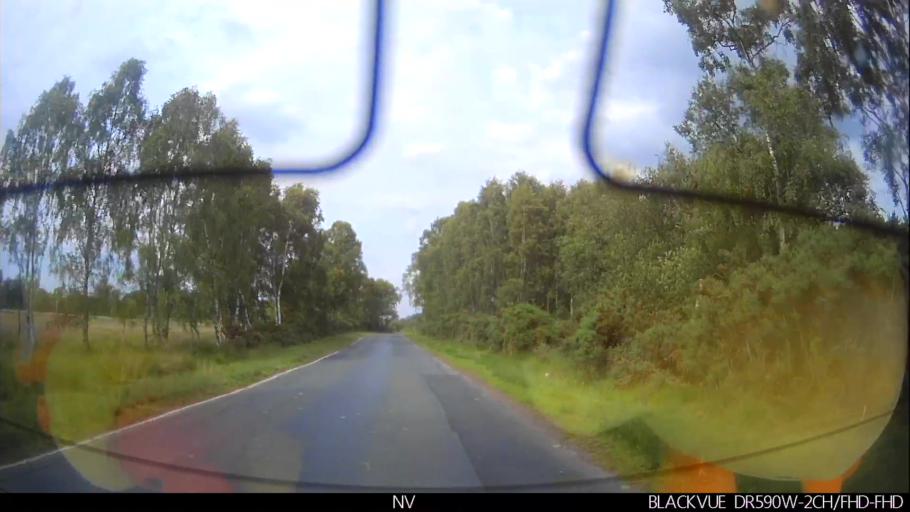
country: GB
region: England
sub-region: North Yorkshire
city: Strensall
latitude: 54.0441
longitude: -1.0094
